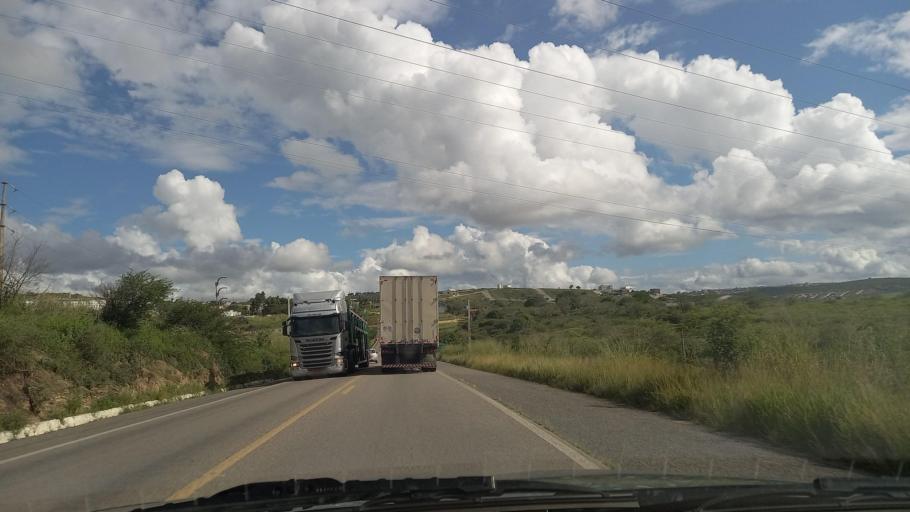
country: BR
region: Pernambuco
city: Garanhuns
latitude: -8.8506
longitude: -36.4616
